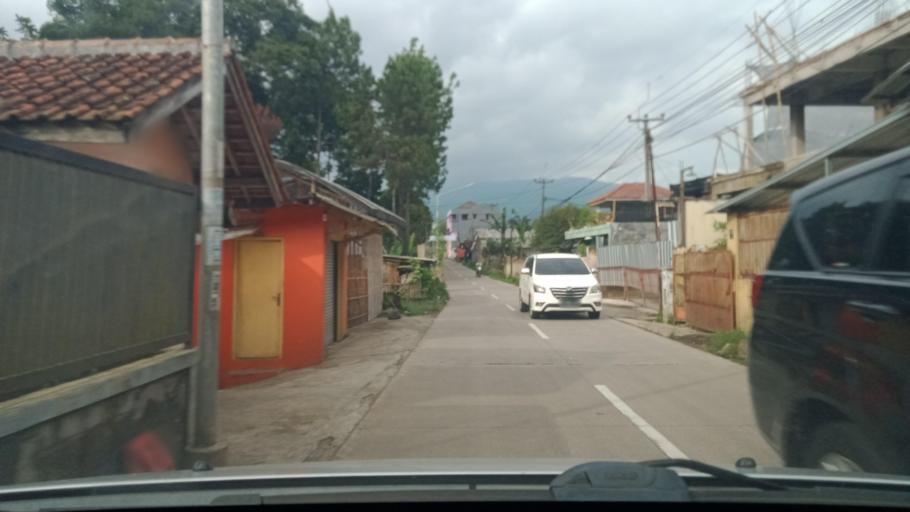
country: ID
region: West Java
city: Lembang
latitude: -6.8160
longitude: 107.5756
